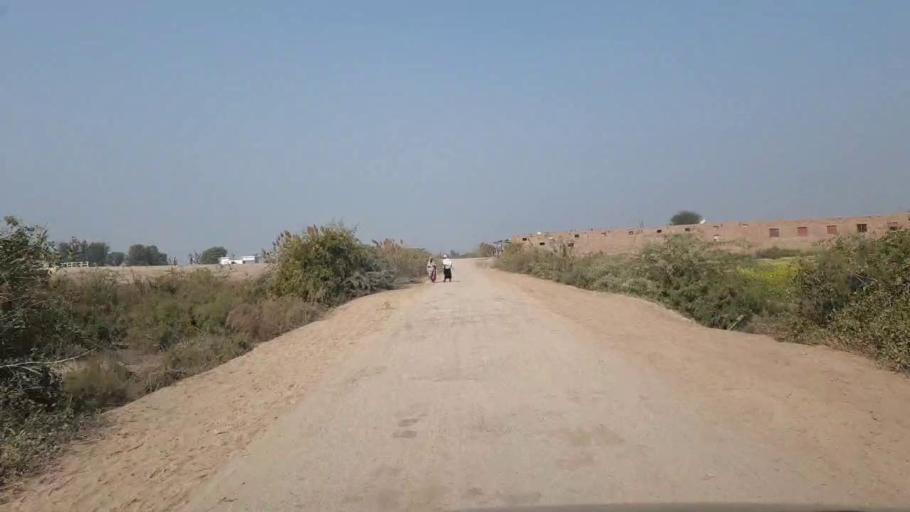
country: PK
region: Sindh
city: Hala
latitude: 25.9526
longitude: 68.4635
